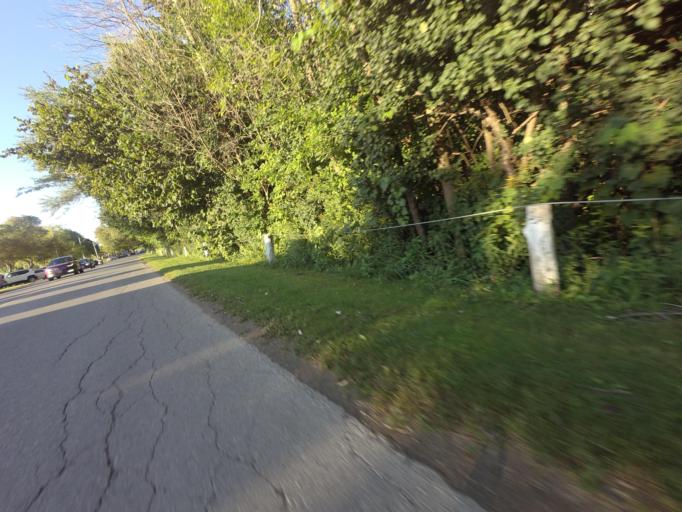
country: CA
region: Ontario
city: Goderich
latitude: 43.7409
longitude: -81.7259
